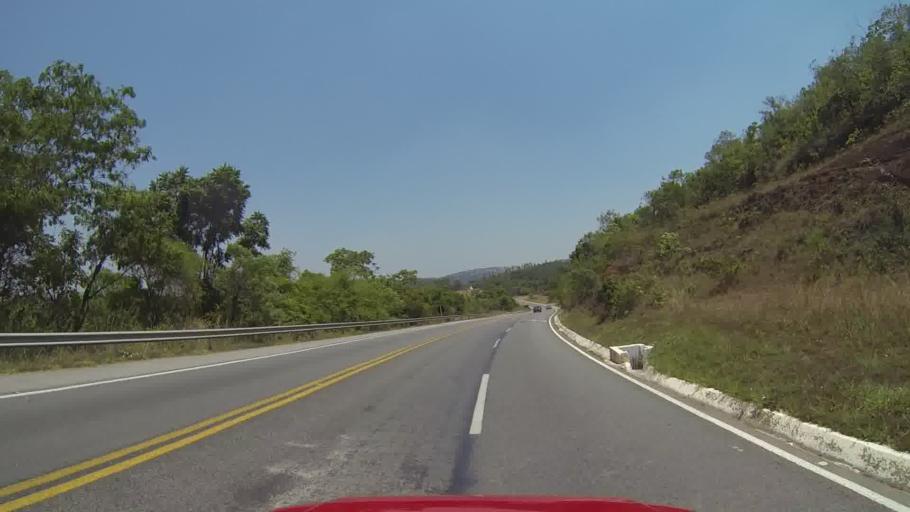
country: BR
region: Minas Gerais
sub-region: Itapecerica
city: Itapecerica
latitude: -20.2807
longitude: -45.1320
